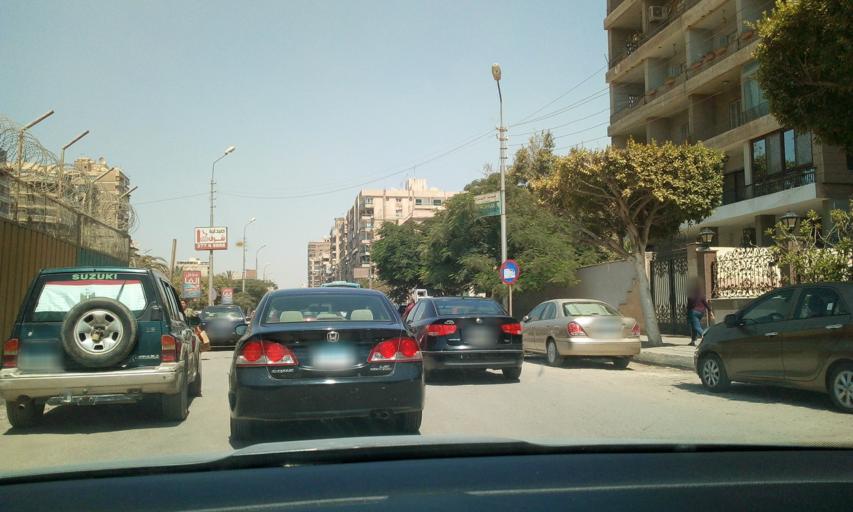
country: EG
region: Muhafazat al Qahirah
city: Cairo
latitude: 30.1085
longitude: 31.3397
